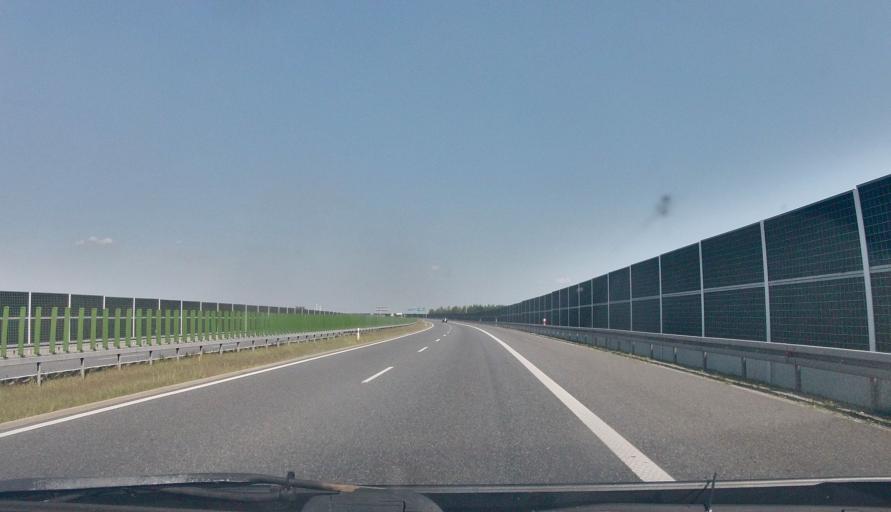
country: PL
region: Lesser Poland Voivodeship
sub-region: Powiat tarnowski
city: Wierzchoslawice
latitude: 50.0079
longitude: 20.8537
